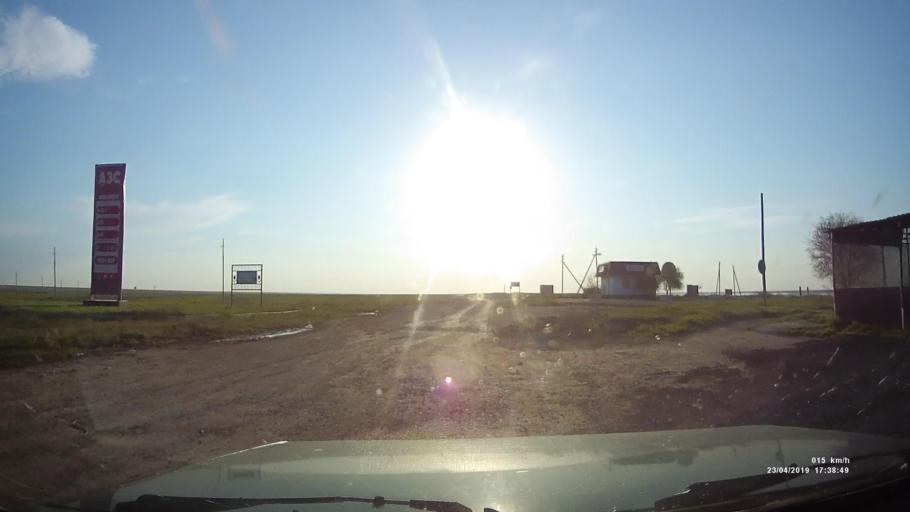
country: RU
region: Kalmykiya
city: Priyutnoye
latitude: 46.0913
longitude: 43.4869
